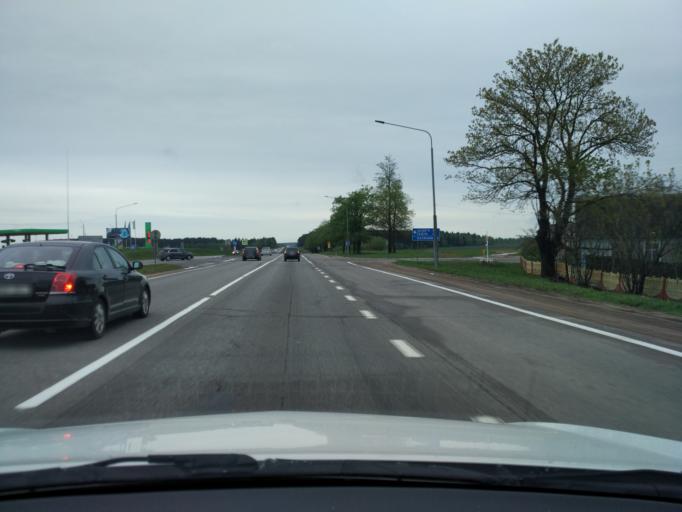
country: BY
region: Minsk
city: Dukora
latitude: 53.7049
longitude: 27.8788
